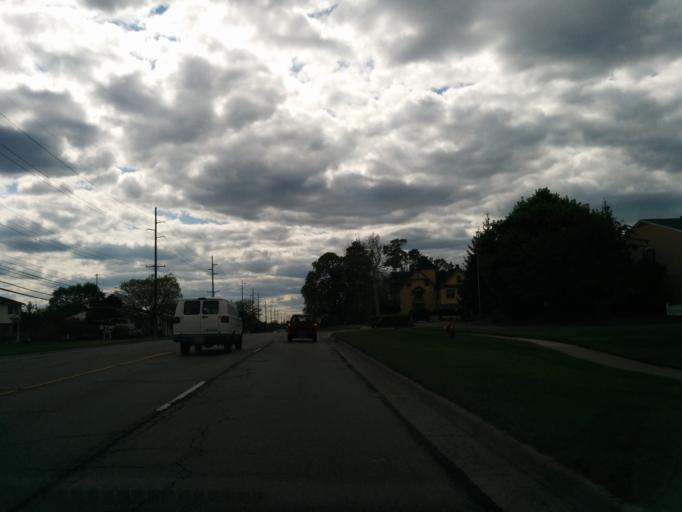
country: US
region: Michigan
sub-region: Oakland County
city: Farmington Hills
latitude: 42.4991
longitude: -83.3663
